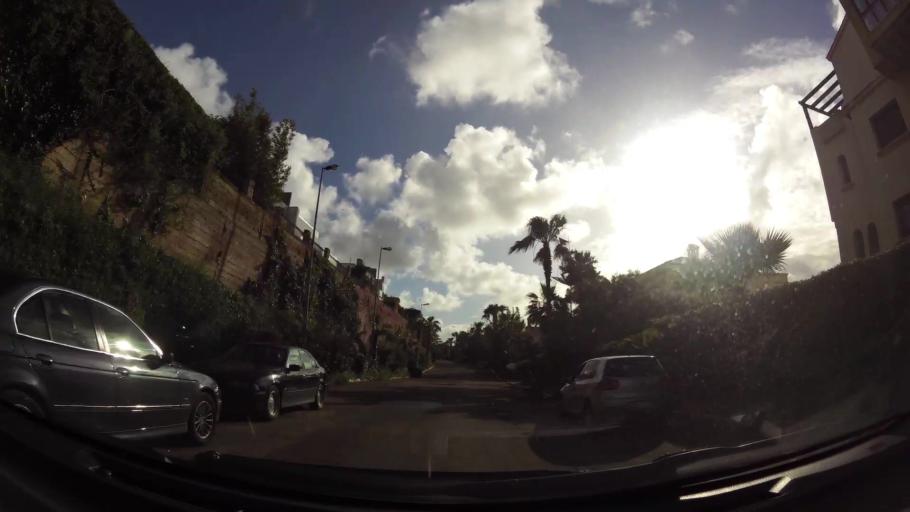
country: MA
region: Grand Casablanca
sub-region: Casablanca
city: Casablanca
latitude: 33.5737
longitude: -7.6899
